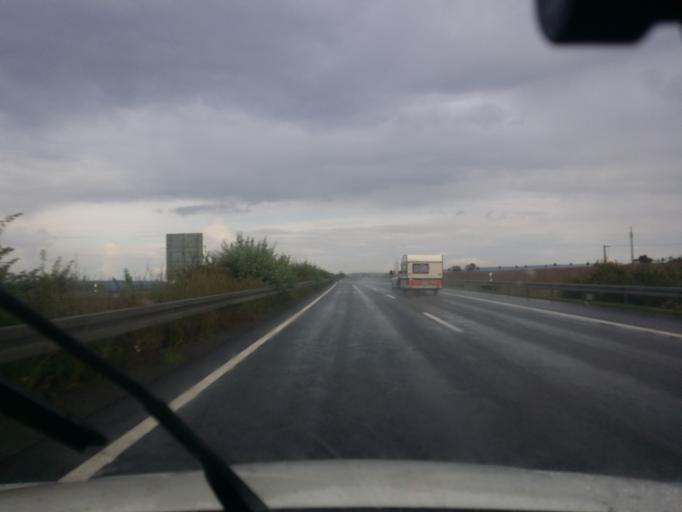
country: DE
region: Thuringia
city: Hausen
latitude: 51.3967
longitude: 10.3549
